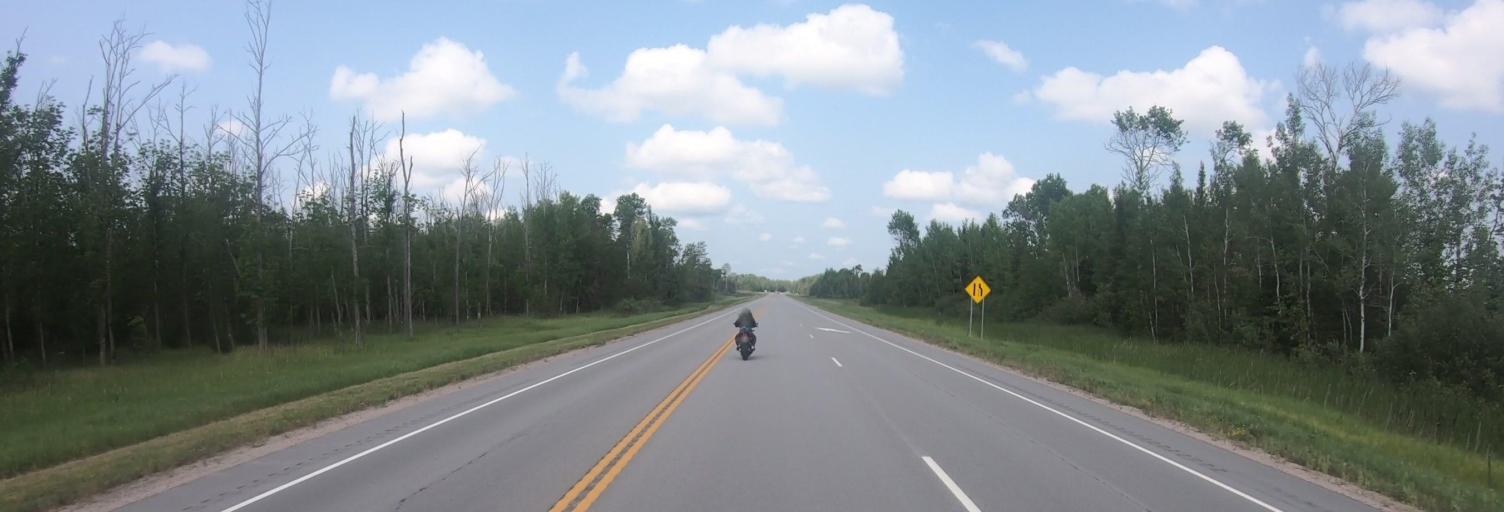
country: US
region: Minnesota
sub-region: Saint Louis County
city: Mountain Iron
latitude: 47.9206
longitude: -92.8172
